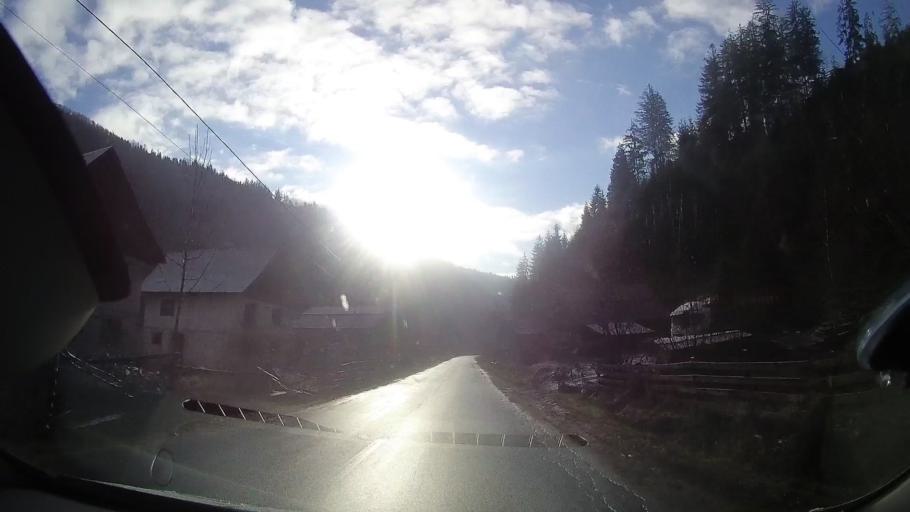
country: RO
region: Alba
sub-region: Comuna Albac
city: Albac
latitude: 46.4420
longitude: 22.9666
